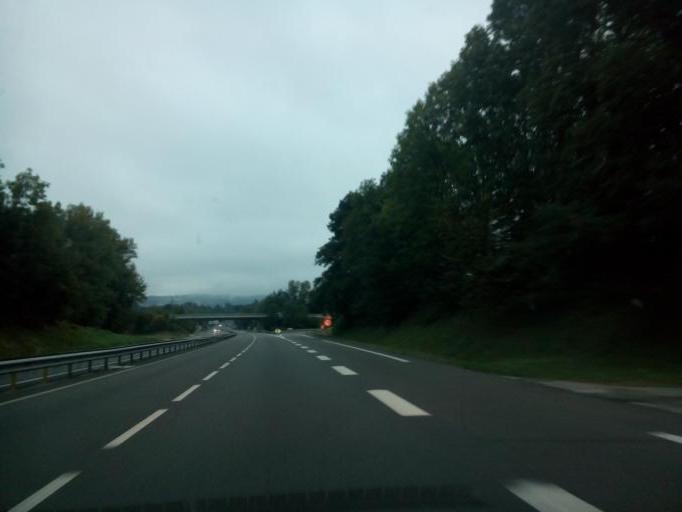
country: FR
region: Rhone-Alpes
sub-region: Departement de l'Isere
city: Chimilin
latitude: 45.5724
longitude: 5.6025
